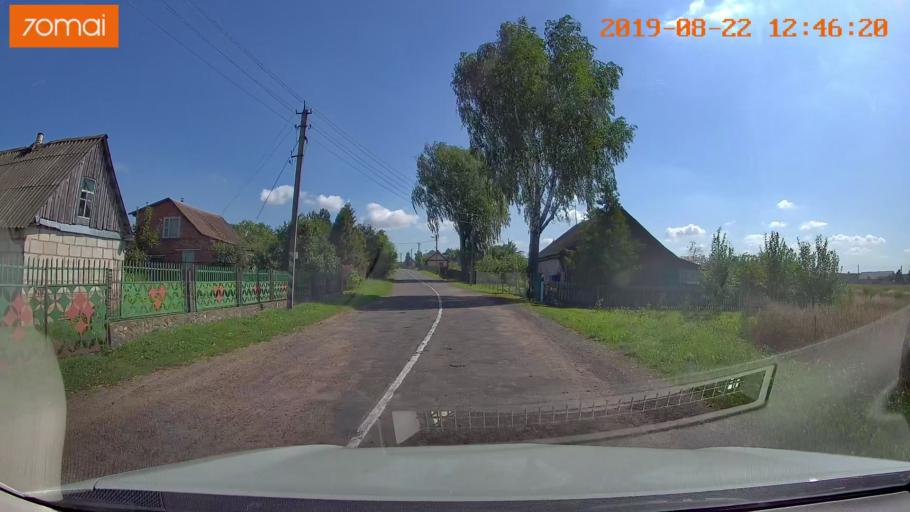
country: BY
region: Minsk
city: Prawdzinski
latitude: 53.4594
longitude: 27.6275
